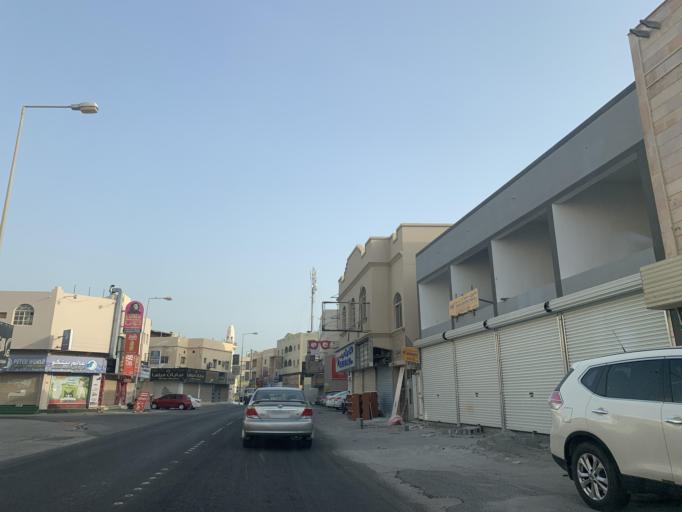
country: BH
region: Northern
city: Madinat `Isa
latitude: 26.1784
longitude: 50.5620
